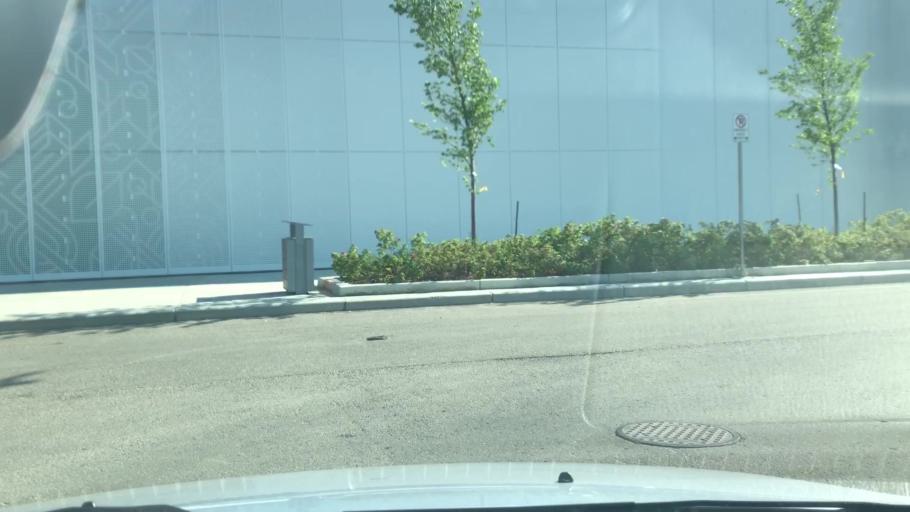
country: CA
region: Alberta
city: Edmonton
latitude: 53.6041
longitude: -113.4453
